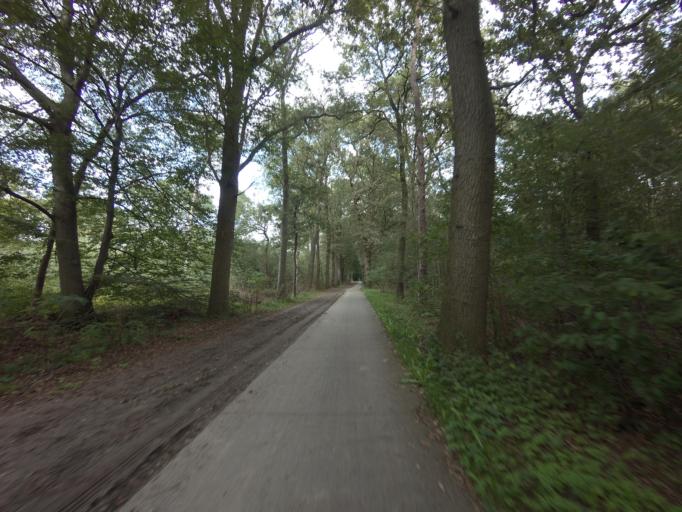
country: NL
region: Drenthe
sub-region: Gemeente Westerveld
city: Dwingeloo
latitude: 52.8025
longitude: 6.3488
